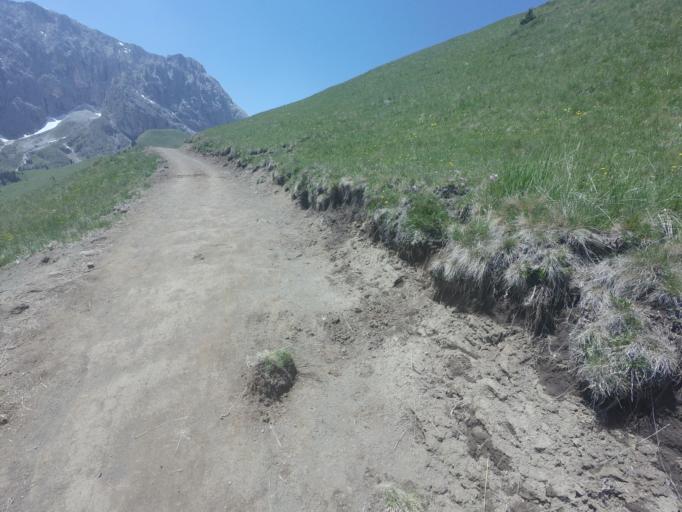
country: IT
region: Trentino-Alto Adige
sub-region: Provincia di Trento
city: Mazzin
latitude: 46.4971
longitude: 11.6655
